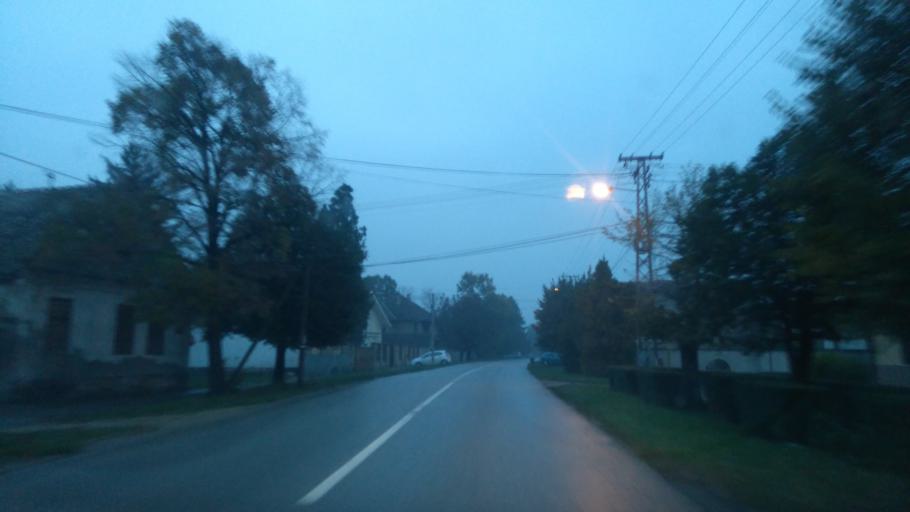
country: RS
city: Backo Petrovo Selo
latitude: 45.7081
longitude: 20.0872
